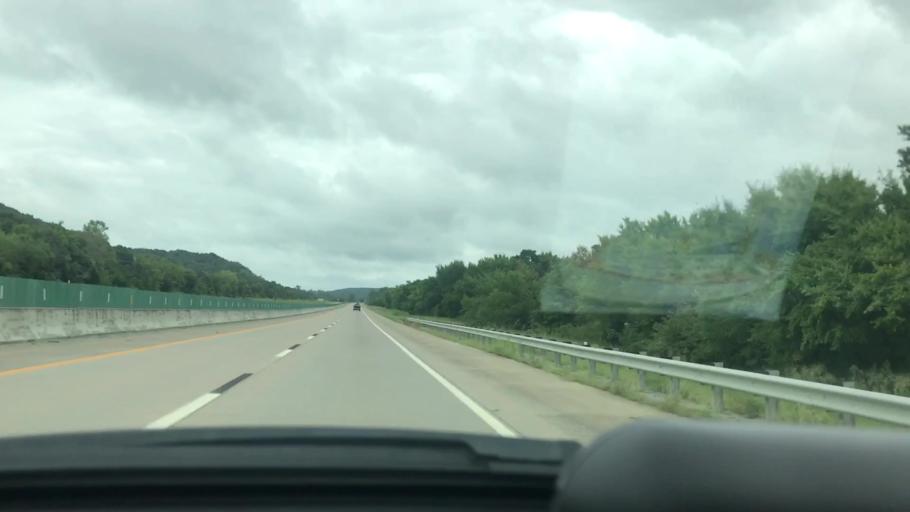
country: US
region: Oklahoma
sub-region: Pittsburg County
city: Krebs
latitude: 35.0837
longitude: -95.7018
